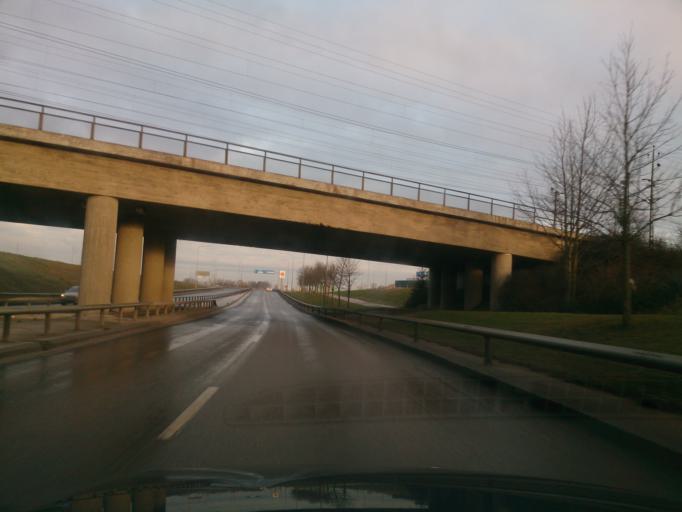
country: SE
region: OEstergoetland
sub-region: Linkopings Kommun
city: Linkoping
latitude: 58.4145
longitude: 15.6550
